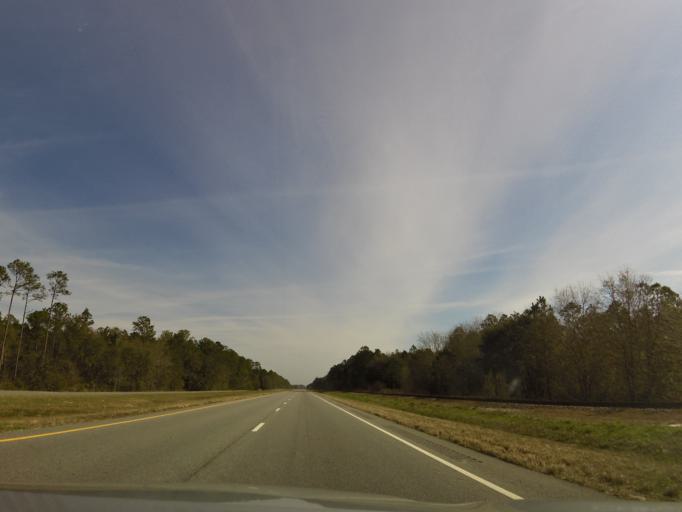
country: US
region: Georgia
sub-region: Lanier County
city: Lakeland
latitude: 30.8927
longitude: -83.1180
